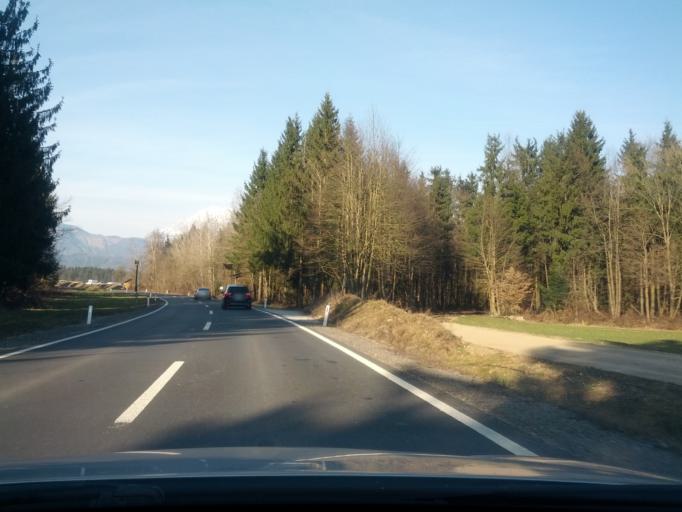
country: SI
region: Sencur
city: Sencur
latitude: 46.2228
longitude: 14.4412
